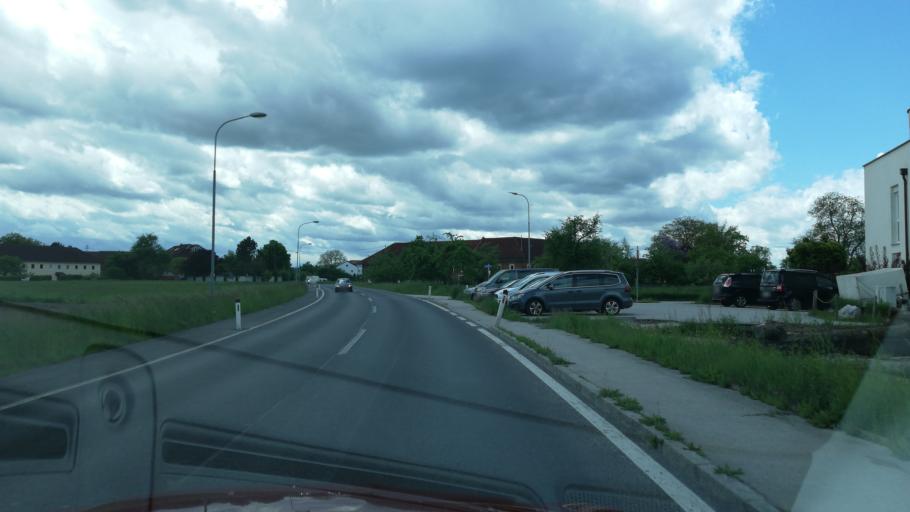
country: AT
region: Upper Austria
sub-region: Politischer Bezirk Linz-Land
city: Ansfelden
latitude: 48.1998
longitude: 14.2625
